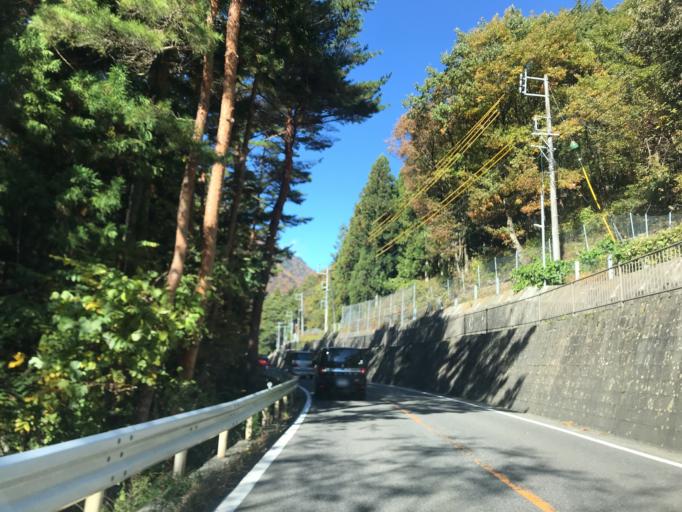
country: JP
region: Nagano
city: Toyoshina
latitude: 36.1836
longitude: 137.7918
